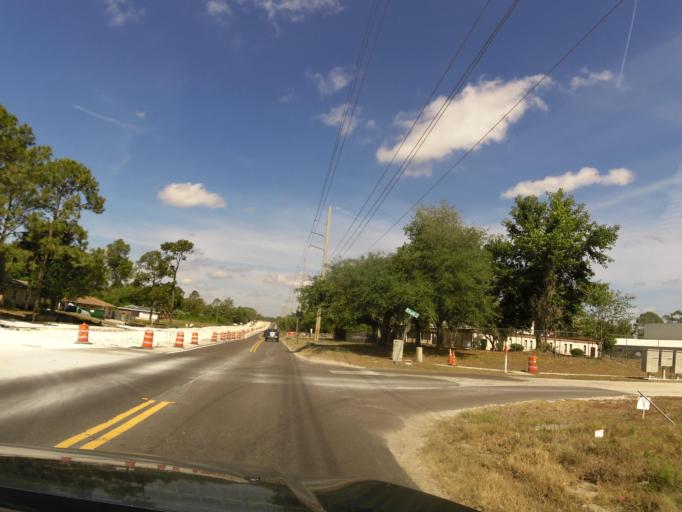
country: US
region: Florida
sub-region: Volusia County
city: Lake Helen
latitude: 28.9281
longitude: -81.1943
